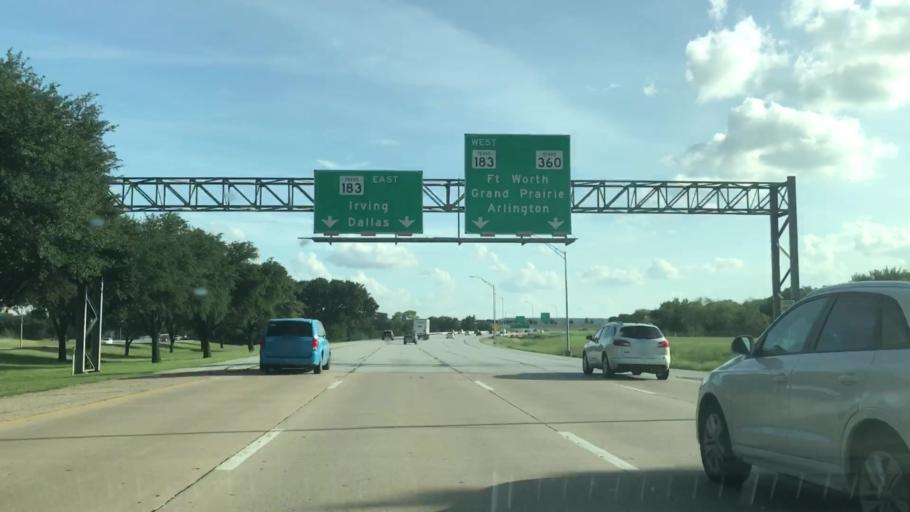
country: US
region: Texas
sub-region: Tarrant County
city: Euless
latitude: 32.8457
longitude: -97.0409
